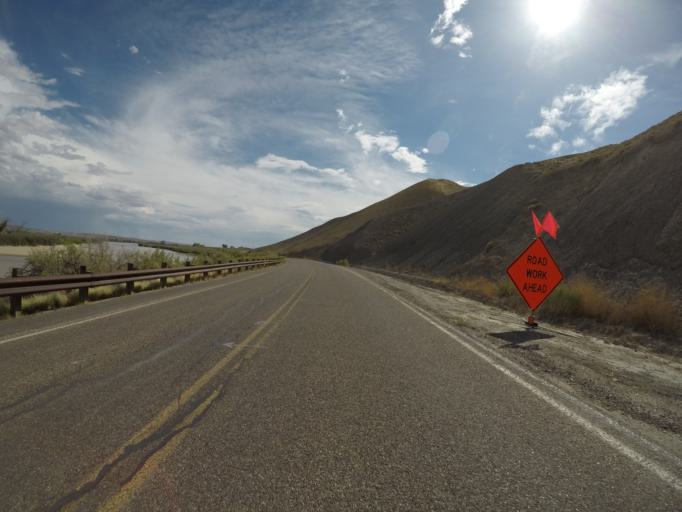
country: US
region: Utah
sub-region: Uintah County
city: Naples
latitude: 40.4358
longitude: -109.3302
